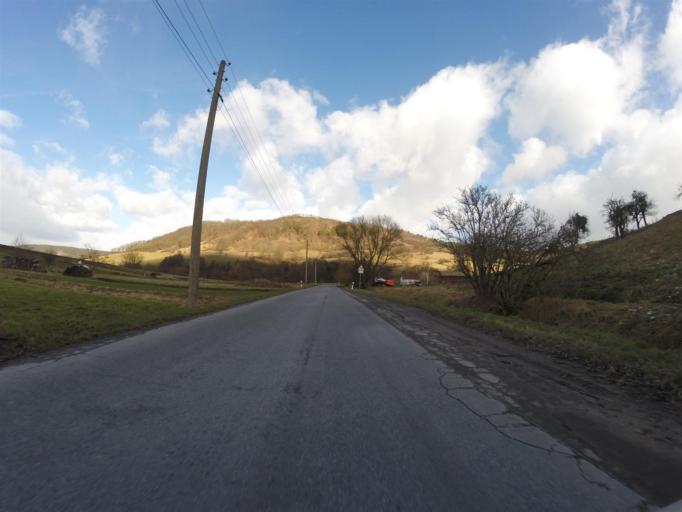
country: DE
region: Thuringia
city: Jenalobnitz
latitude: 50.9507
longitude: 11.6948
